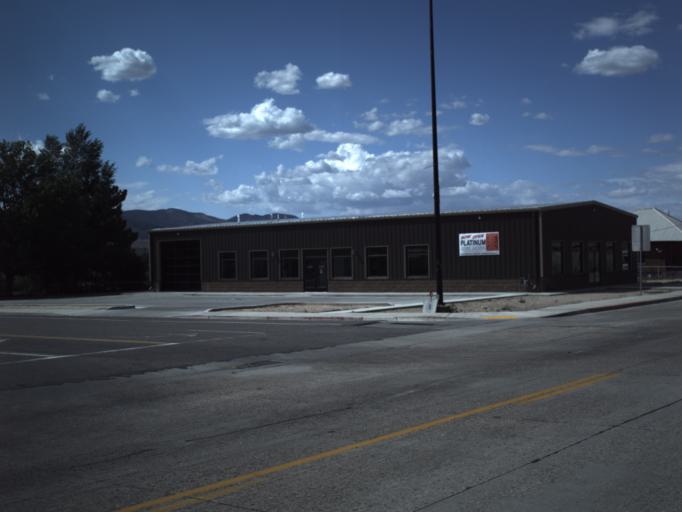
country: US
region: Utah
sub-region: Sevier County
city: Salina
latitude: 38.9632
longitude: -111.8600
